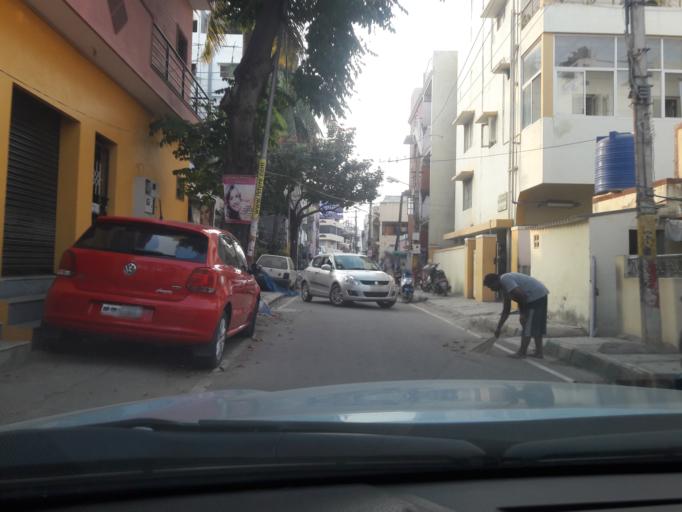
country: IN
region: Karnataka
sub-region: Bangalore Urban
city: Bangalore
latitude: 13.0100
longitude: 77.6251
